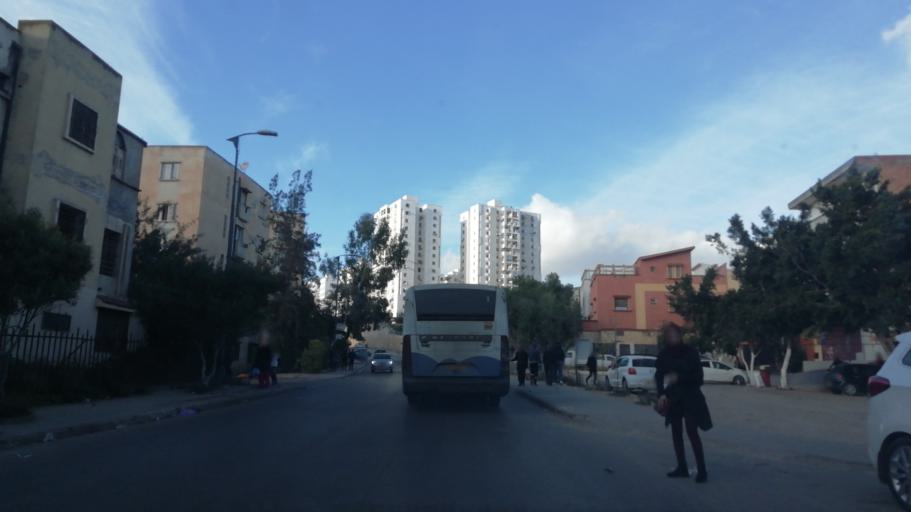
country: DZ
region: Oran
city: Bir el Djir
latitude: 35.6981
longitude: -0.5739
